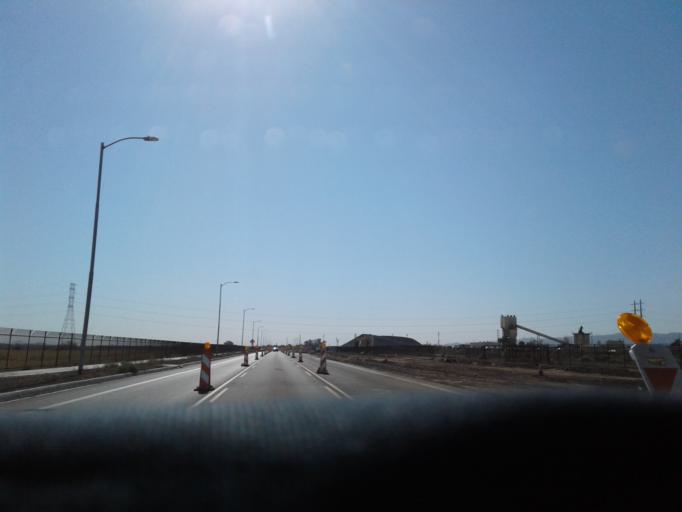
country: US
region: Arizona
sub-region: Maricopa County
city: Laveen
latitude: 33.4034
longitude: -112.1651
